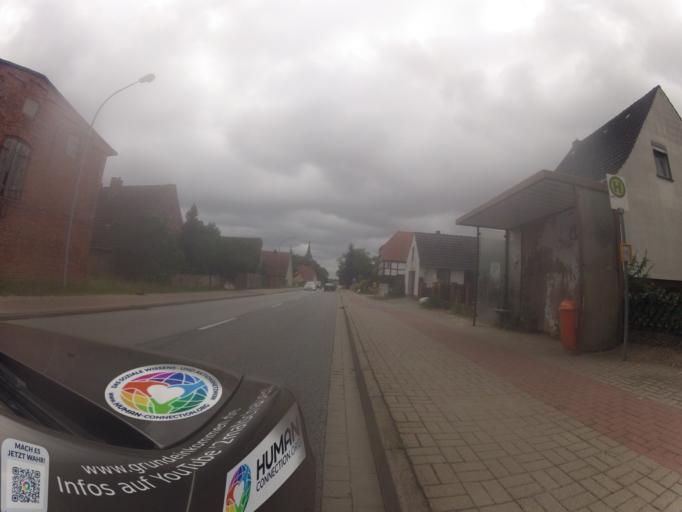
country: DE
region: Mecklenburg-Vorpommern
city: Jatznick
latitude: 53.5459
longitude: 13.9691
